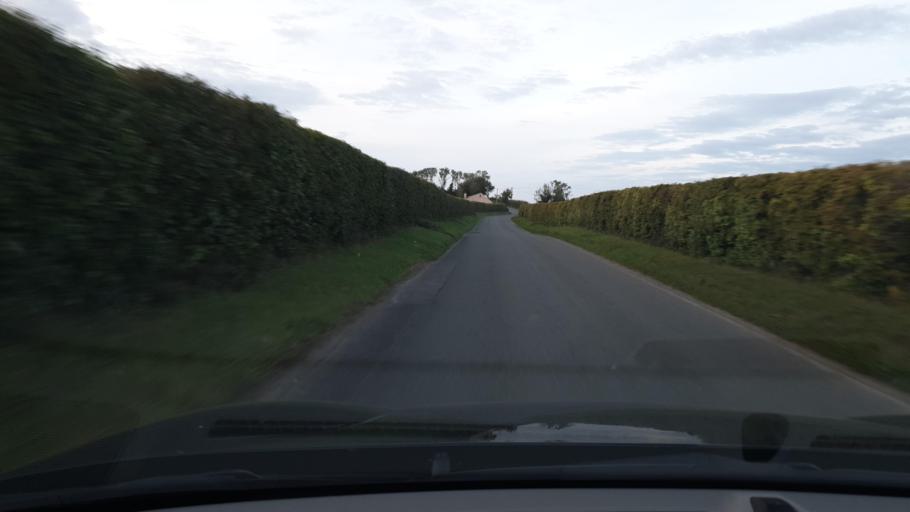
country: IE
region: Leinster
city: Lusk
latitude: 53.5602
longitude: -6.1666
